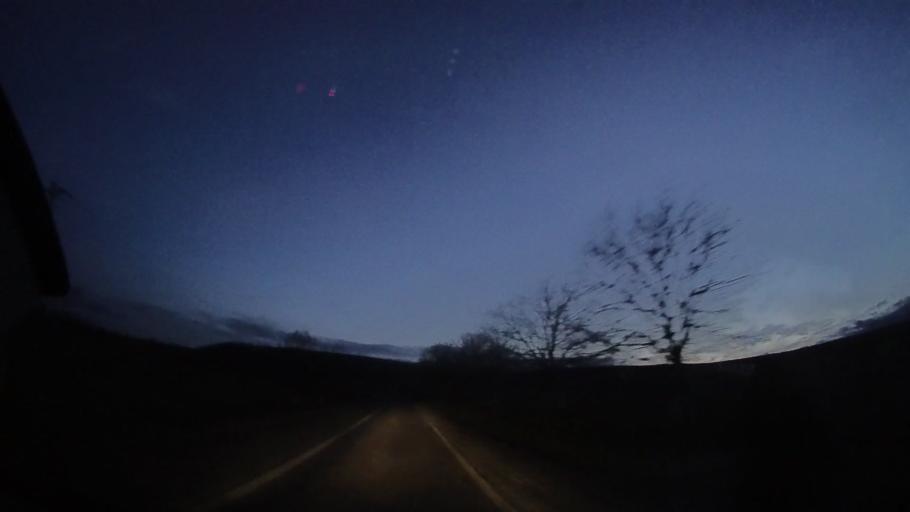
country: RO
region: Mures
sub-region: Comuna Sarmasu
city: Sarmasu
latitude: 46.7770
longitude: 24.2256
